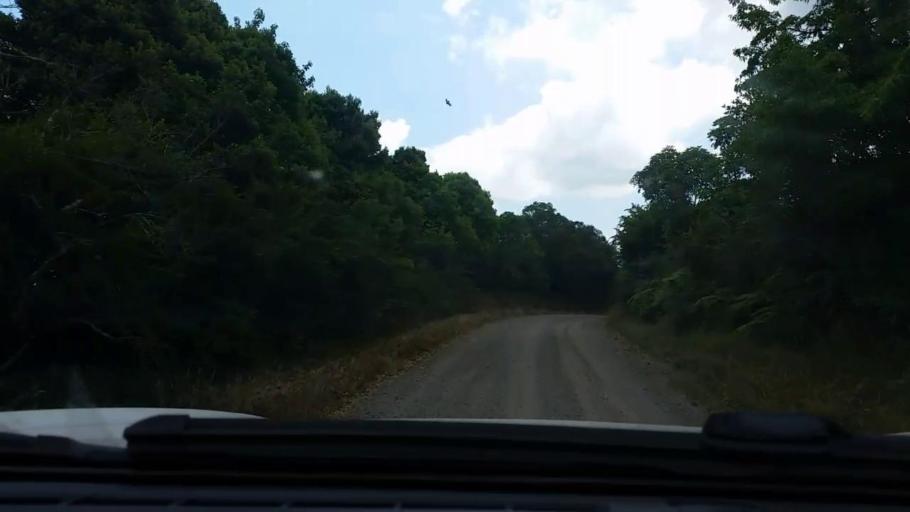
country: NZ
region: Bay of Plenty
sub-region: Kawerau District
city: Kawerau
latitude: -38.0152
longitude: 176.5765
